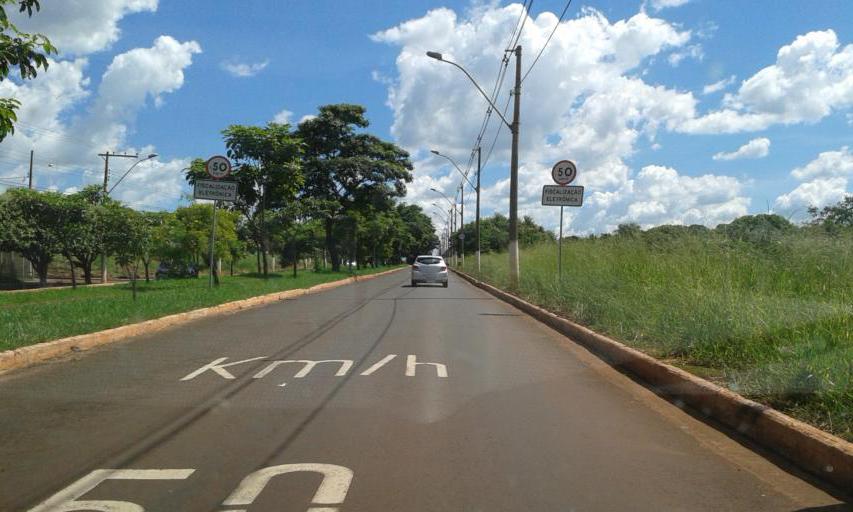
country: BR
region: Minas Gerais
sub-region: Ituiutaba
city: Ituiutaba
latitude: -18.9668
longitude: -49.4726
